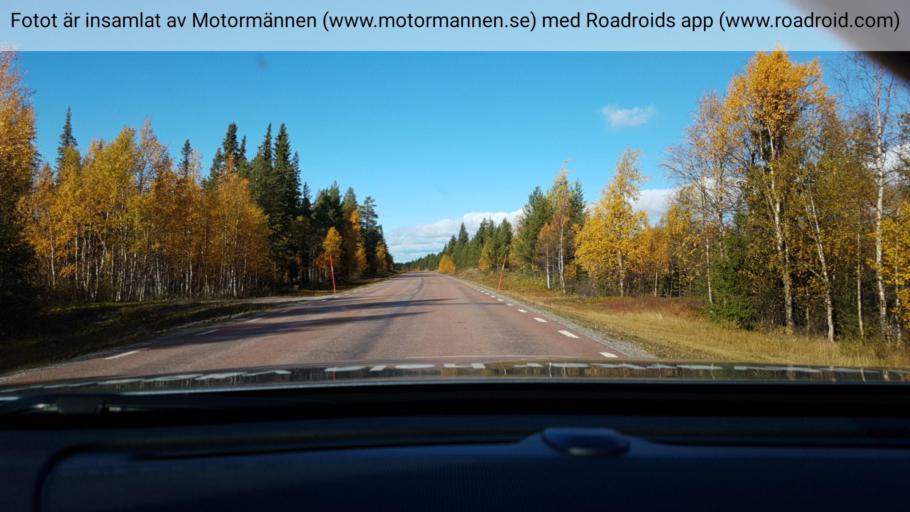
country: SE
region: Norrbotten
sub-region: Arjeplogs Kommun
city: Arjeplog
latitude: 65.9917
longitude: 18.1793
